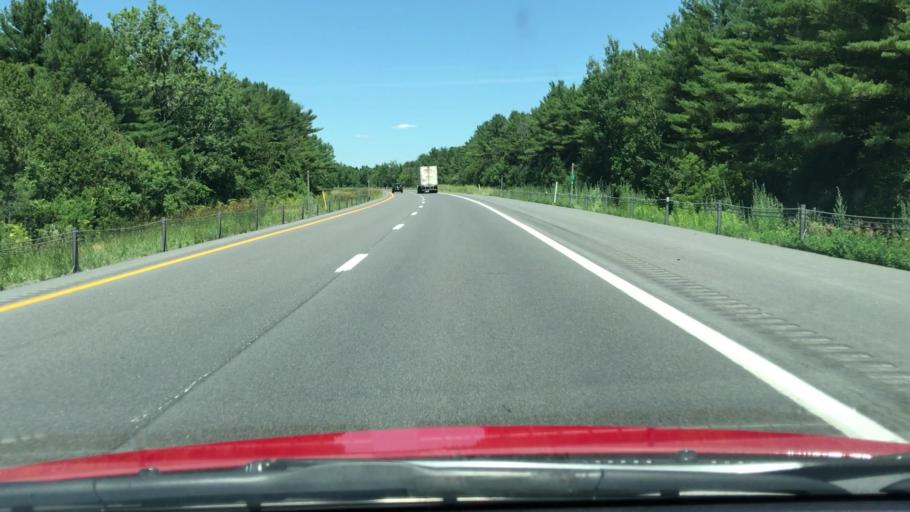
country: US
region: New York
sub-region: Clinton County
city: Cumberland Head
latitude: 44.7476
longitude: -73.4273
